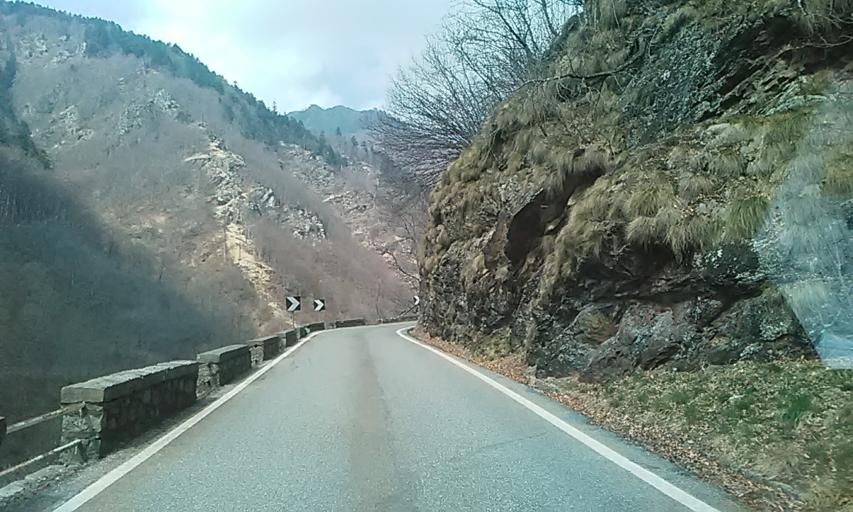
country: IT
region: Piedmont
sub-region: Provincia di Vercelli
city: Rimella
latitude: 45.9032
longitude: 8.1802
